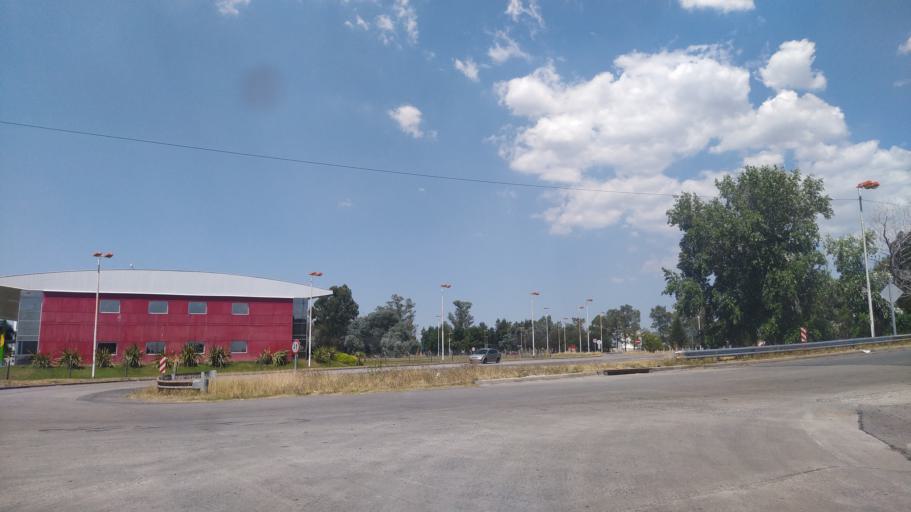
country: AR
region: Buenos Aires
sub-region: Partido de Ezeiza
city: Ezeiza
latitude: -34.9039
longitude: -58.6225
